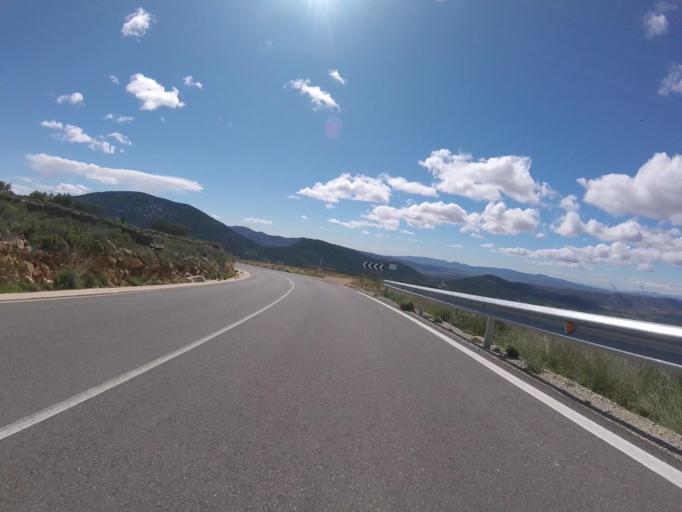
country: ES
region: Valencia
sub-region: Provincia de Castello
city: Culla
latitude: 40.3003
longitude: -0.1265
